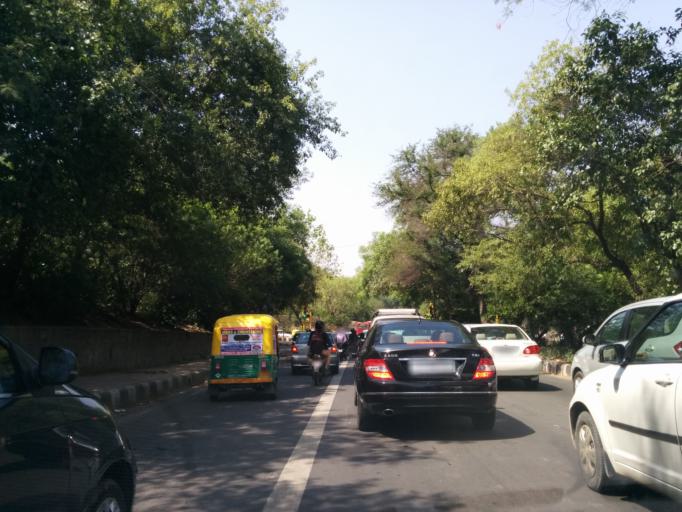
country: IN
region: NCT
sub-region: New Delhi
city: New Delhi
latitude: 28.5325
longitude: 77.1955
